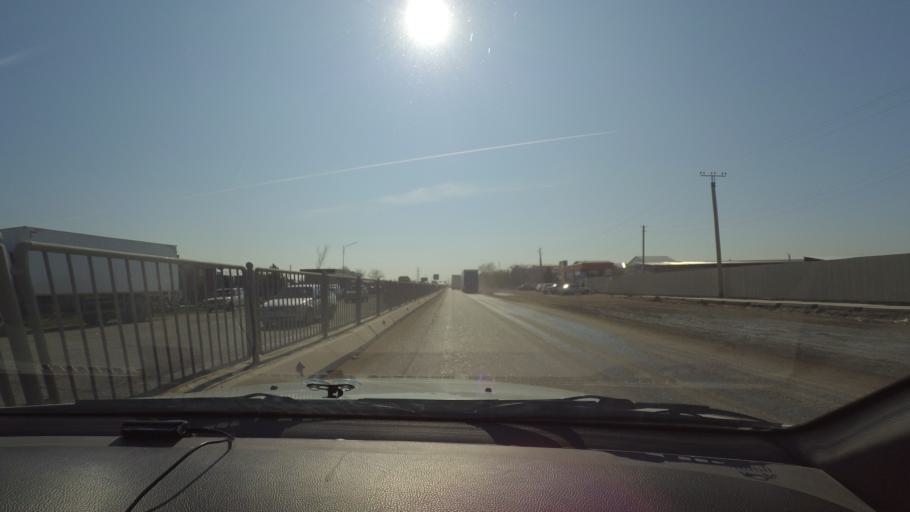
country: UZ
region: Bukhara
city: Bukhara
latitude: 39.8065
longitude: 64.4222
